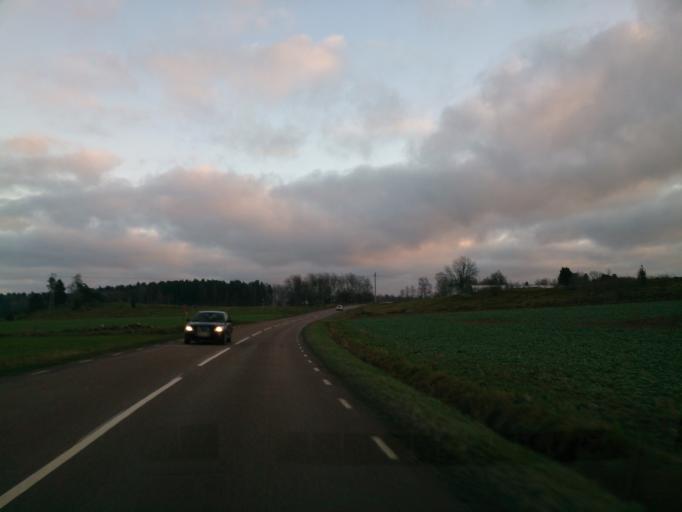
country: SE
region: OEstergoetland
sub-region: Linkopings Kommun
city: Linghem
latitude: 58.4313
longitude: 15.9008
